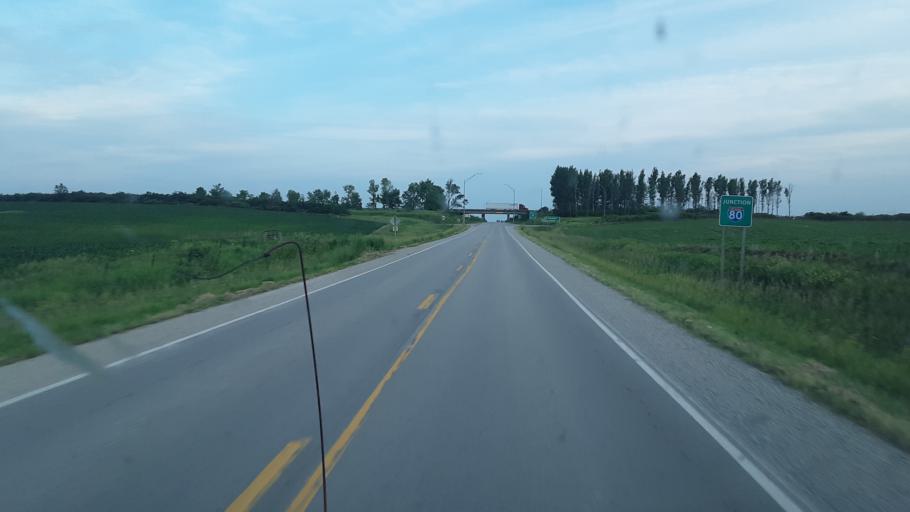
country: US
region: Iowa
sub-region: Iowa County
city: Marengo
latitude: 41.6995
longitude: -92.1625
